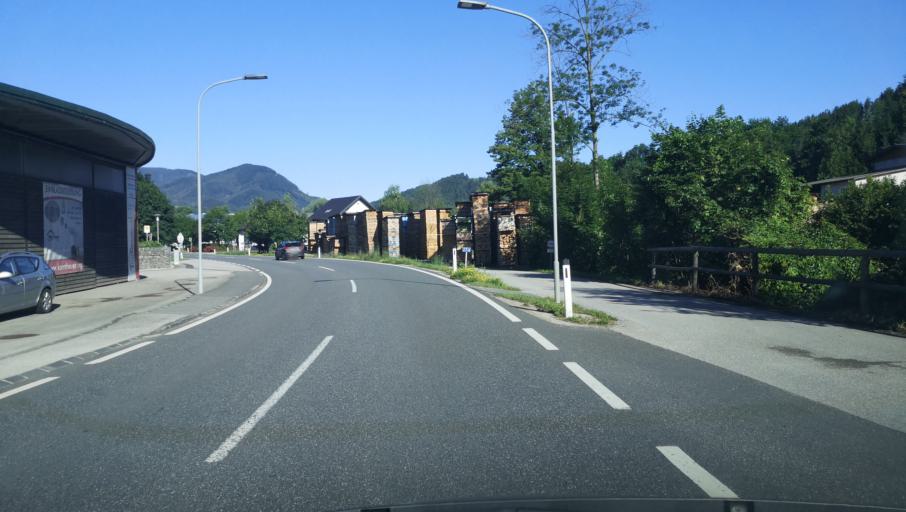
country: AT
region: Lower Austria
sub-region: Politischer Bezirk Amstetten
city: Ybbsitz
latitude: 47.9434
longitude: 14.8325
